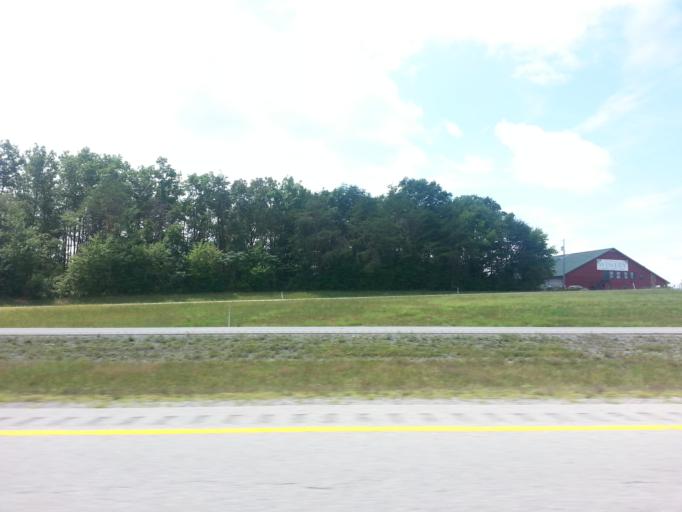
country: US
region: Tennessee
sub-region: Cumberland County
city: Crossville
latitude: 35.9616
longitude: -84.9813
